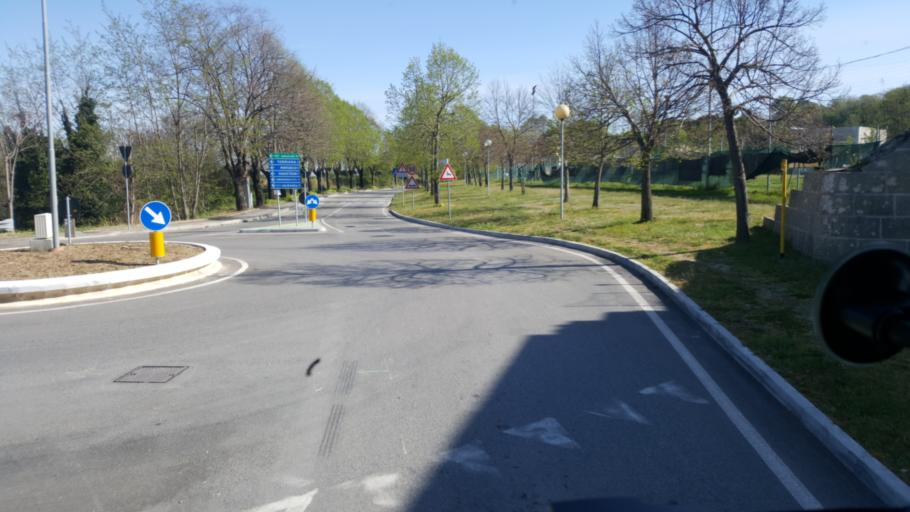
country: IT
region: Emilia-Romagna
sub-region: Provincia di Rimini
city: Verucchio
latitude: 43.9820
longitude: 12.4071
